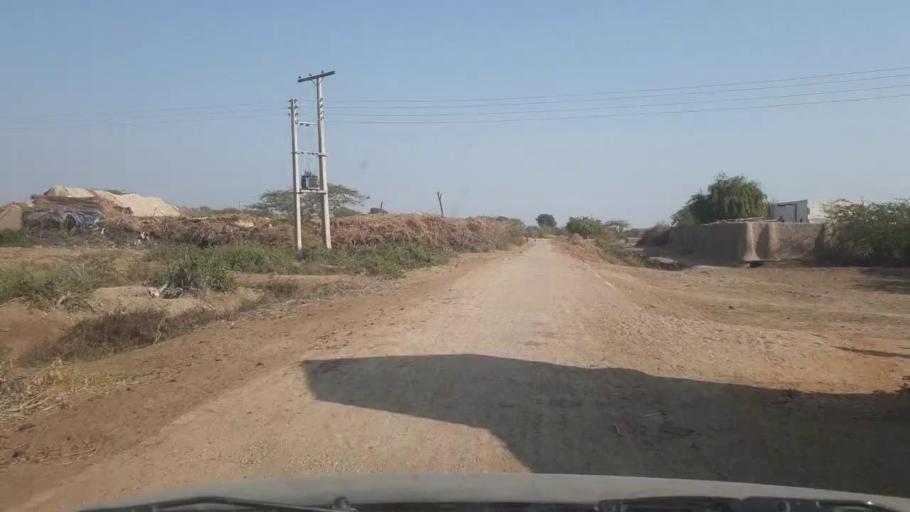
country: PK
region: Sindh
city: Samaro
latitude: 25.1837
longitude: 69.3659
